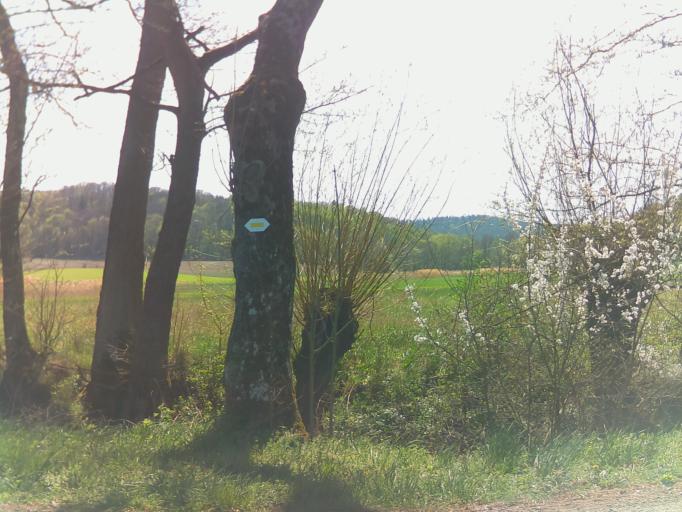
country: DE
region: Bavaria
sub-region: Upper Franconia
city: Weitramsdorf
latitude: 50.3009
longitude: 10.7969
